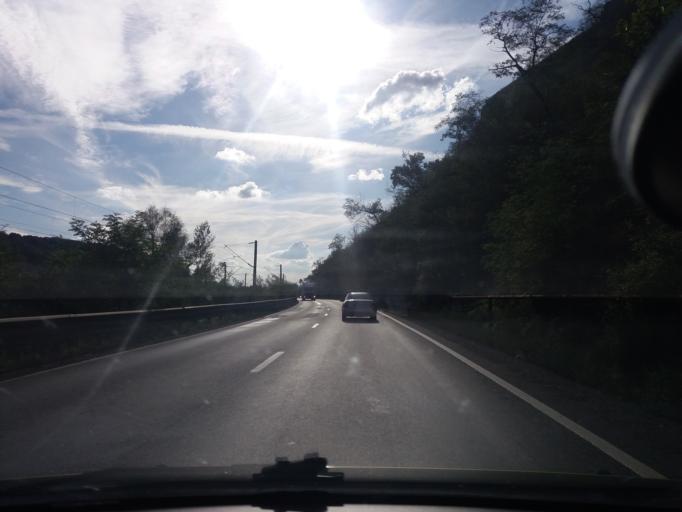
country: RO
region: Arad
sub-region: Oras Lipova
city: Lipova
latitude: 46.1084
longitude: 21.7266
